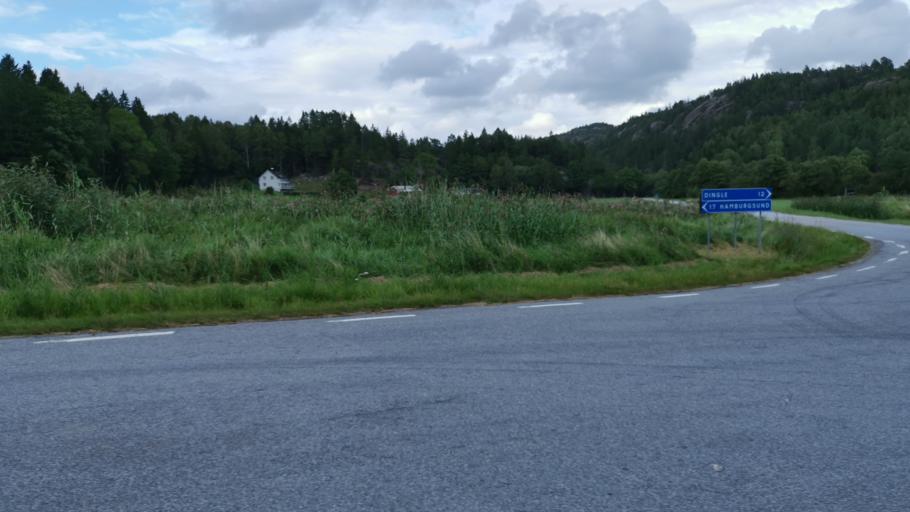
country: SE
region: Vaestra Goetaland
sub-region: Lysekils Kommun
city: Brastad
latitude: 58.4687
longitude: 11.4607
